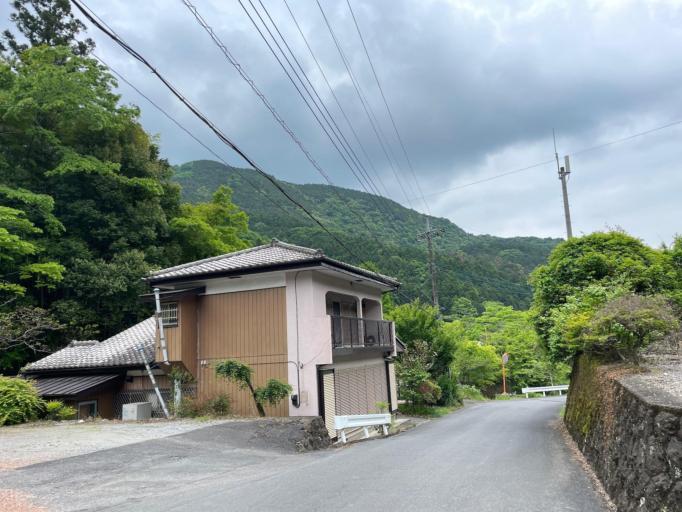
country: JP
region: Tochigi
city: Tanuma
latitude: 36.4733
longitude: 139.5942
